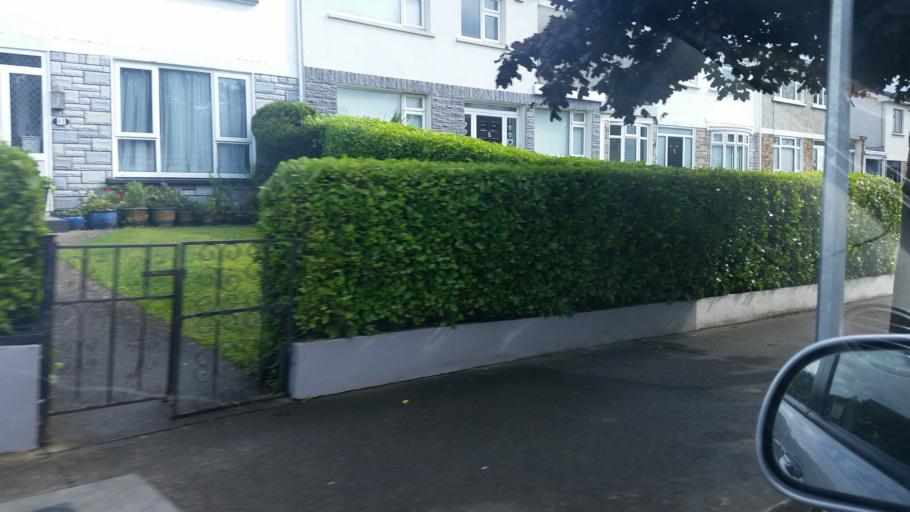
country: IE
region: Leinster
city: Portmarnock
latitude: 53.4337
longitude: -6.1301
